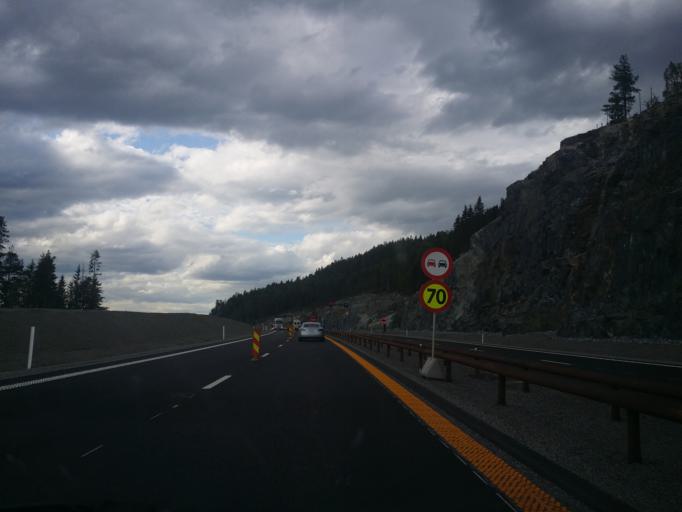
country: NO
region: Akershus
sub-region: Eidsvoll
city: Eidsvoll
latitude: 60.4278
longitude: 11.2411
